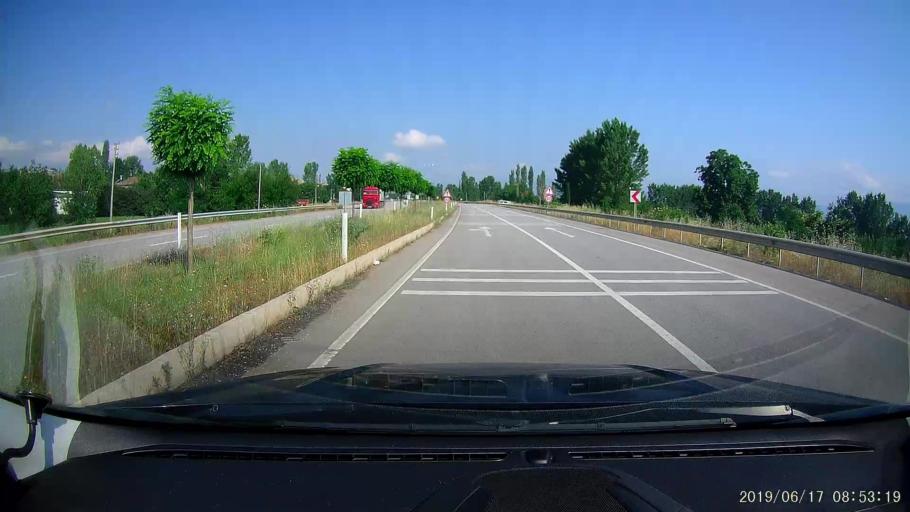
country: TR
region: Tokat
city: Erbaa
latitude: 40.7087
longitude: 36.4834
